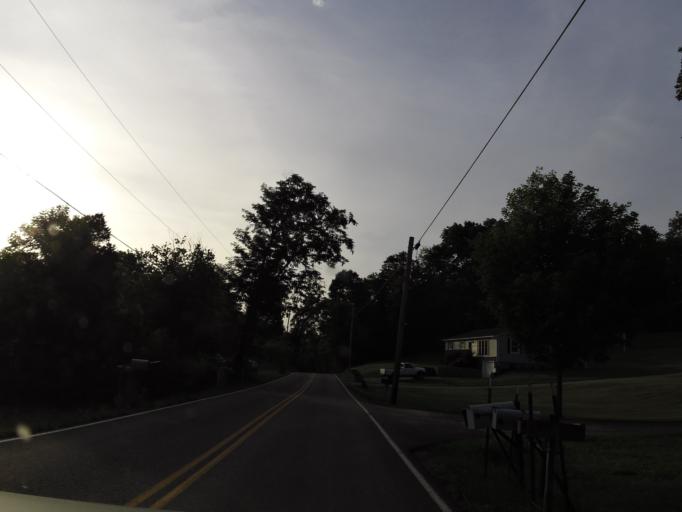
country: US
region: Tennessee
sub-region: Sevier County
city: Seymour
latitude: 35.9108
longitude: -83.8110
